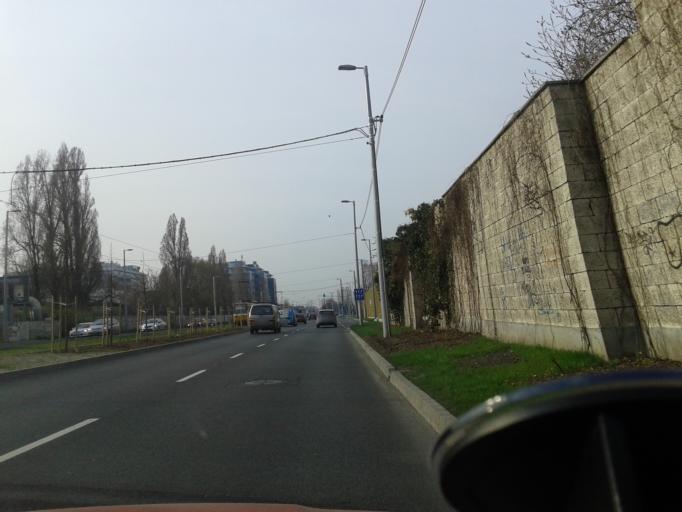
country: HU
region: Budapest
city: Budapest XI. keruelet
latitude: 47.4643
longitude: 19.0488
